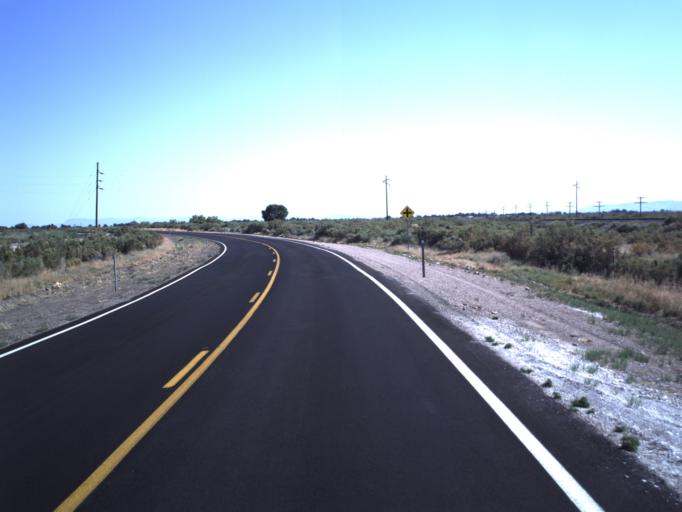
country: US
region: Utah
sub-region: Millard County
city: Delta
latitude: 39.2550
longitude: -112.6537
